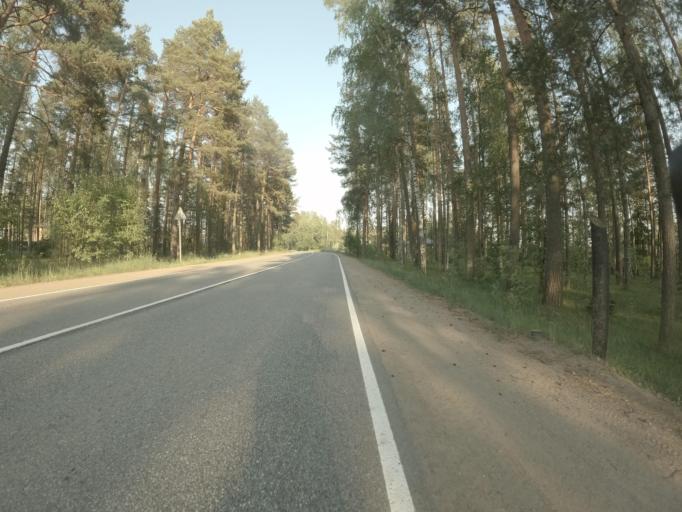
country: RU
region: Leningrad
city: Veshchevo
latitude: 60.4720
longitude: 29.2656
